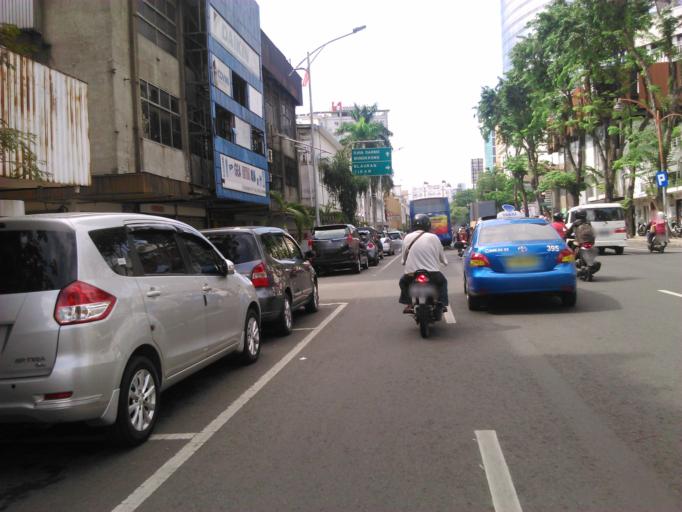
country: ID
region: East Java
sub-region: Kota Surabaya
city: Surabaya
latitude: -7.2595
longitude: 112.7391
